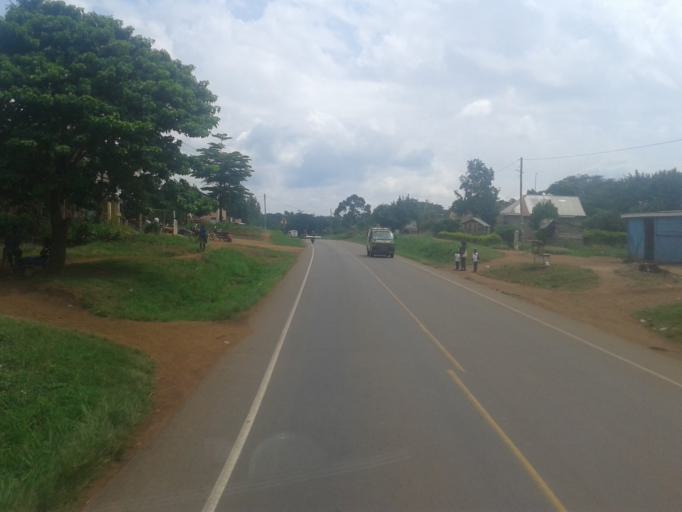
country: UG
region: Central Region
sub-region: Luwero District
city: Luwero
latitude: 0.8759
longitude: 32.4845
